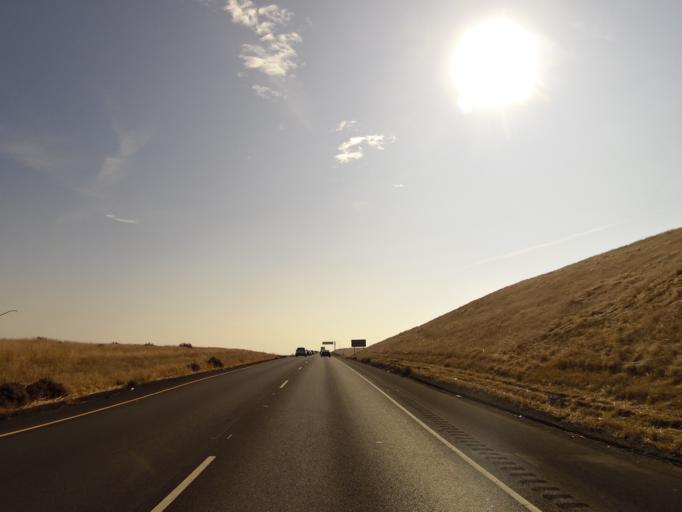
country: US
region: California
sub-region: Kings County
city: Kettleman City
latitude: 35.9869
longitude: -119.9660
